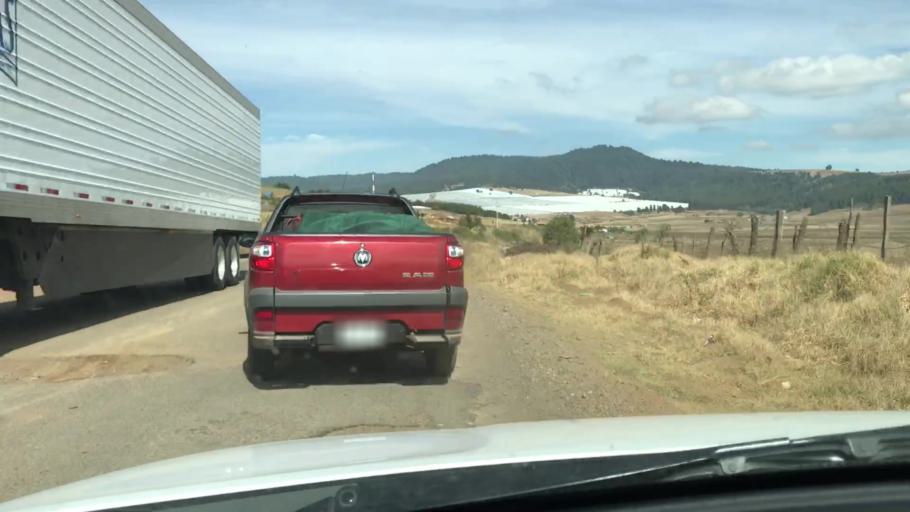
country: MX
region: Jalisco
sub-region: Amacueca
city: Tepec
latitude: 20.0142
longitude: -103.6950
